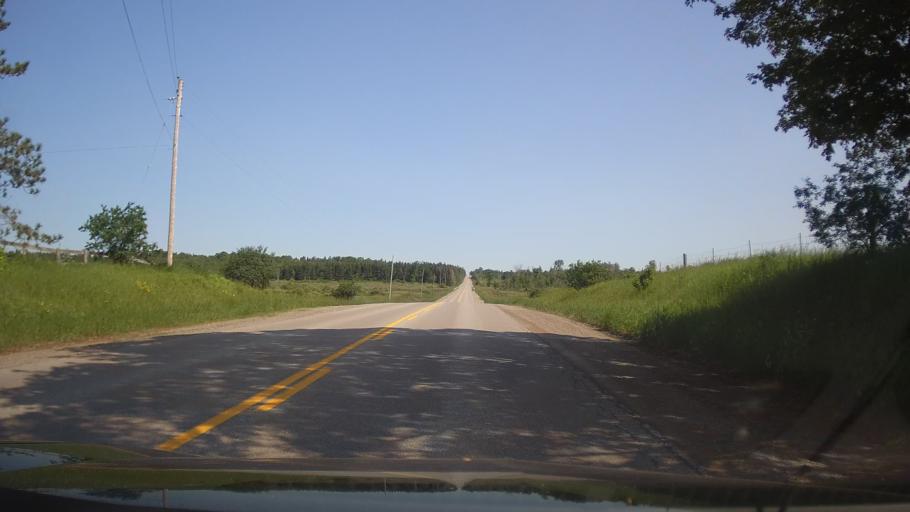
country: CA
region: Ontario
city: Uxbridge
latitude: 44.4769
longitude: -78.9390
